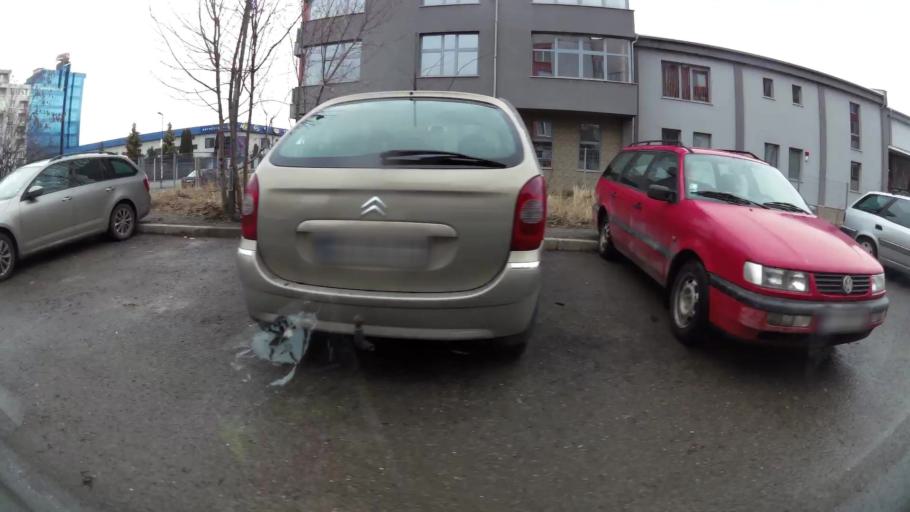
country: BG
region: Sofiya
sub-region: Obshtina Bozhurishte
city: Bozhurishte
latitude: 42.7294
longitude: 23.2542
